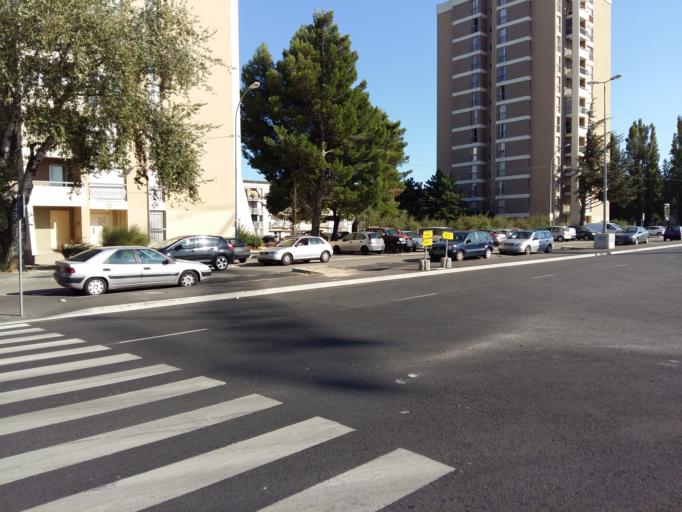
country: FR
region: Provence-Alpes-Cote d'Azur
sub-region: Departement du Vaucluse
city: Montfavet
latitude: 43.9317
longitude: 4.8407
